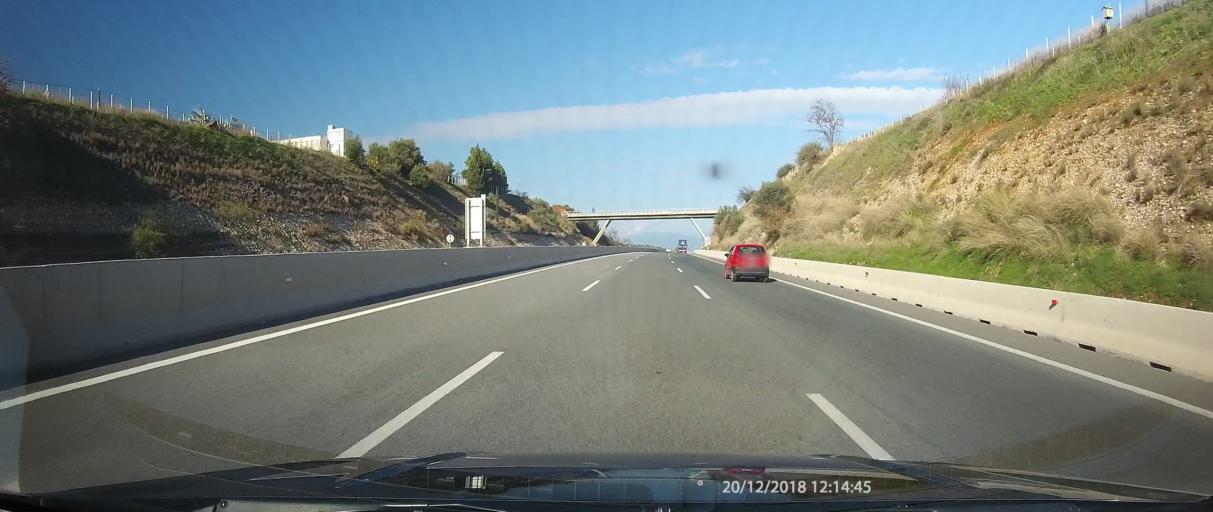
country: GR
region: West Greece
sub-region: Nomos Achaias
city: Aigio
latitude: 38.2408
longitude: 22.0752
